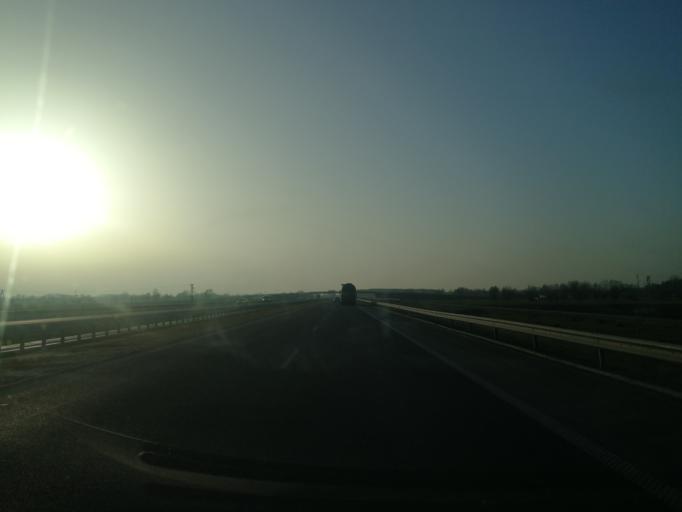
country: PL
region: Warmian-Masurian Voivodeship
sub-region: Powiat elblaski
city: Gronowo Elblaskie
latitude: 54.1644
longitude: 19.2785
